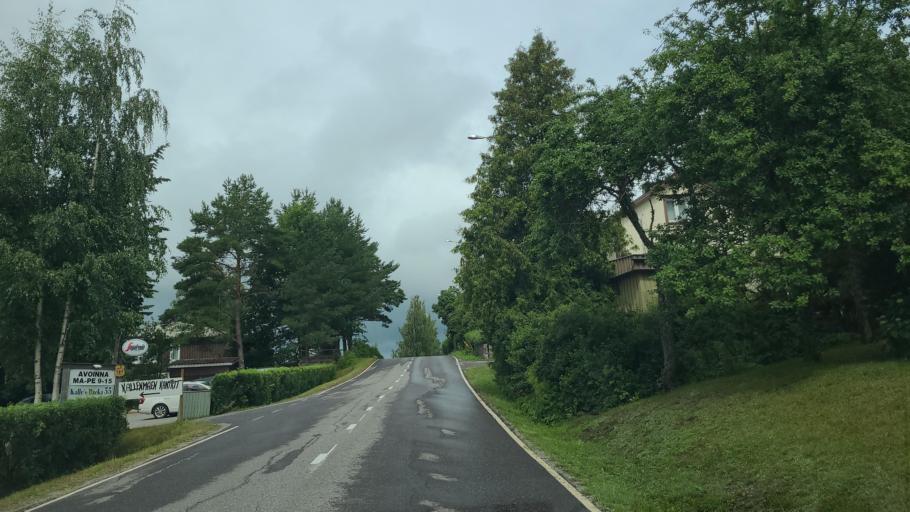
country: FI
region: Varsinais-Suomi
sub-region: Turku
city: Sauvo
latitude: 60.3365
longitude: 22.7047
